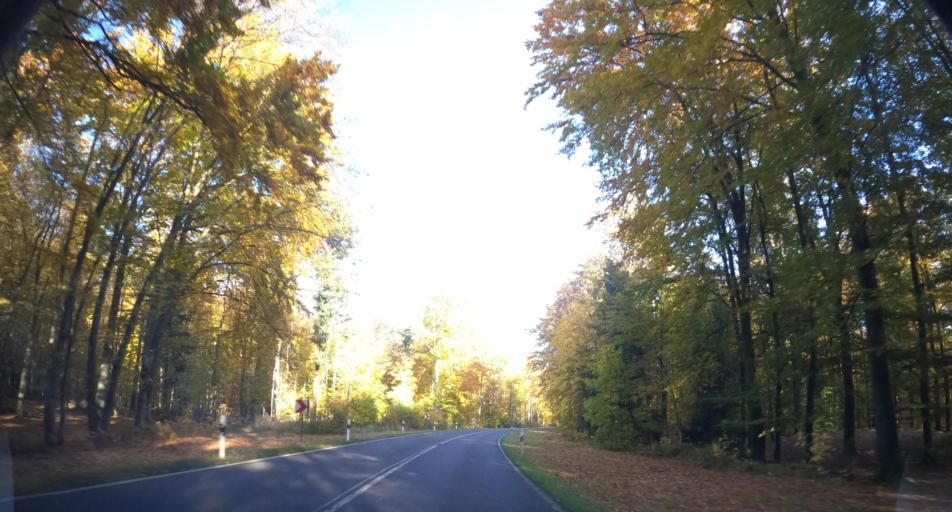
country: DE
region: Mecklenburg-Vorpommern
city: Ahlbeck
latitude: 53.6733
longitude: 14.1344
